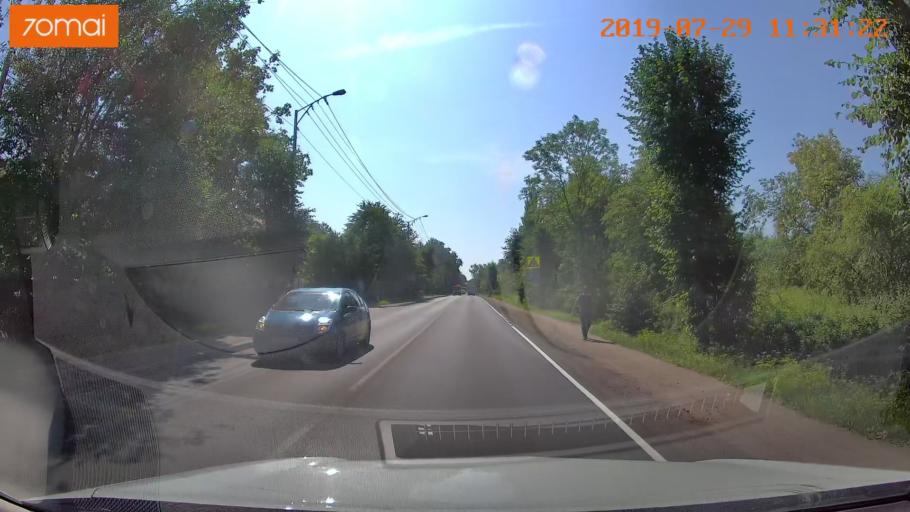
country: RU
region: Kaliningrad
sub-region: Gorod Kaliningrad
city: Kaliningrad
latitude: 54.6755
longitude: 20.5412
